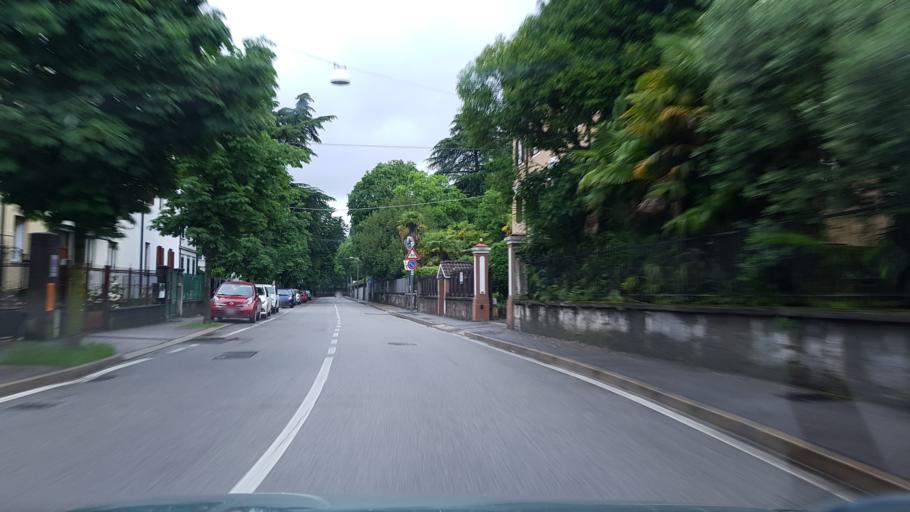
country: IT
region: Friuli Venezia Giulia
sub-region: Provincia di Gorizia
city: Gorizia
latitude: 45.9512
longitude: 13.6213
